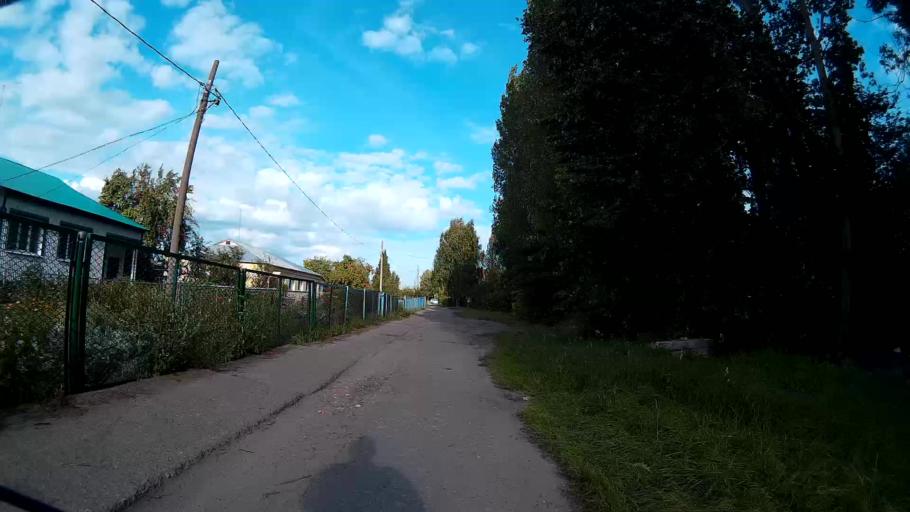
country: RU
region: Ulyanovsk
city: Isheyevka
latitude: 54.2889
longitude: 48.2044
